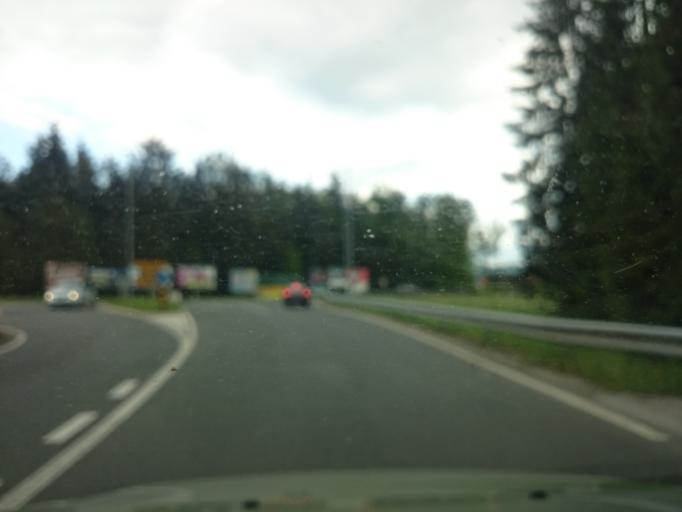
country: SI
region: Sentjur pri Celju
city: Sentjur
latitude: 46.2616
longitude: 15.3928
